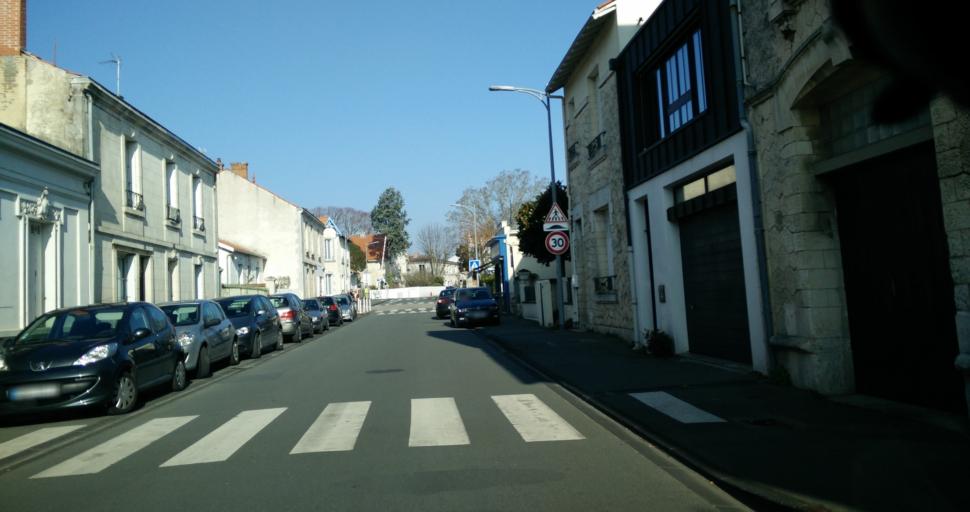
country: FR
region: Poitou-Charentes
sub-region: Departement de la Charente-Maritime
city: La Rochelle
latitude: 46.1651
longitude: -1.1593
